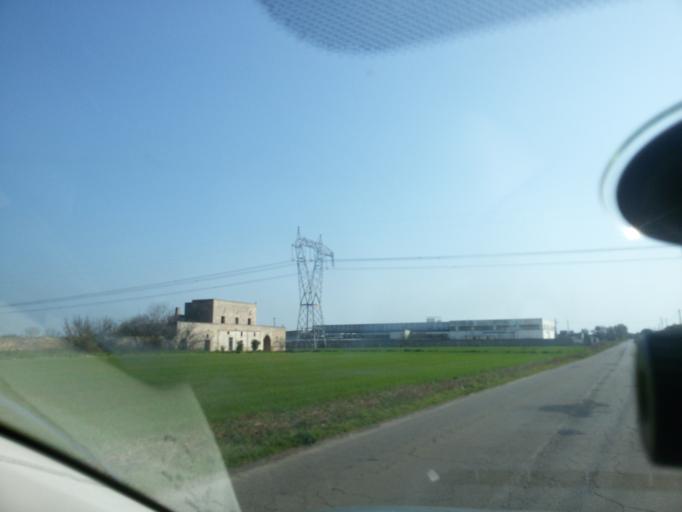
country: IT
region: Apulia
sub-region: Provincia di Brindisi
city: Mesagne
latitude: 40.5823
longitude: 17.8128
